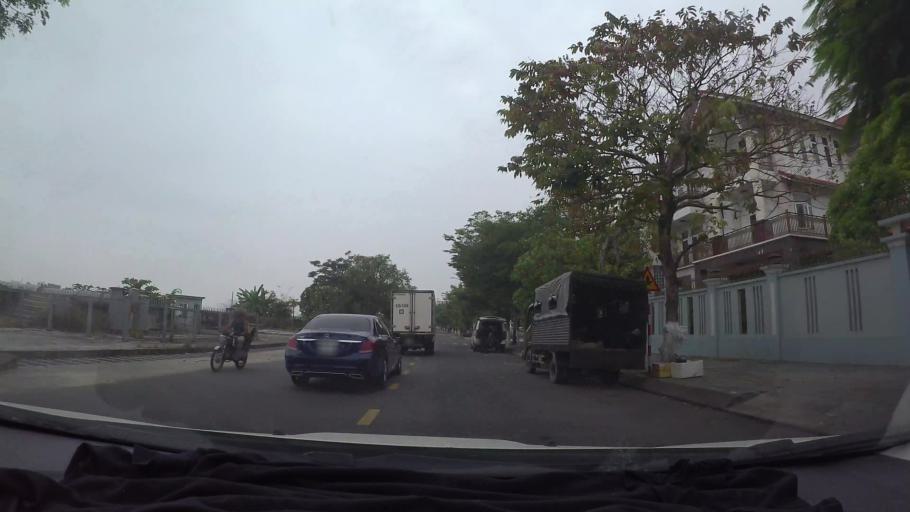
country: VN
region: Da Nang
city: Cam Le
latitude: 16.0294
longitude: 108.2272
